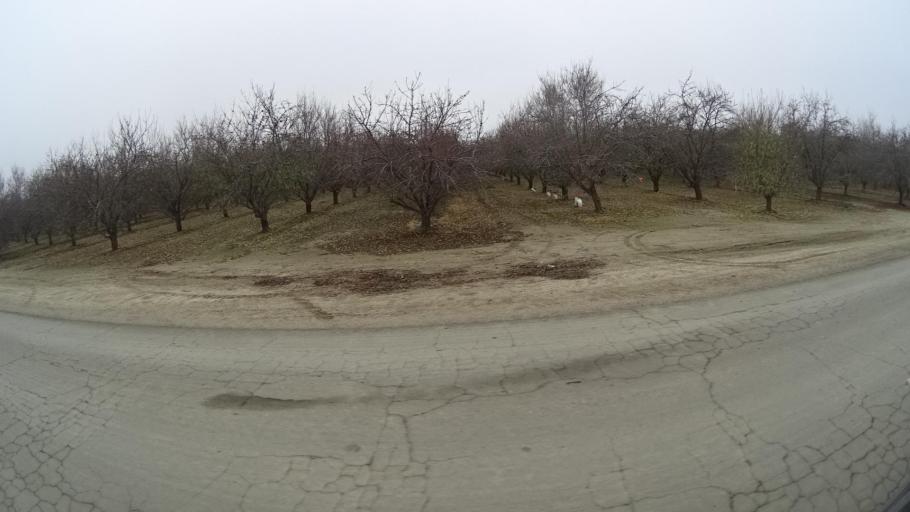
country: US
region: California
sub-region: Kern County
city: Greenfield
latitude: 35.2380
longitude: -119.1030
